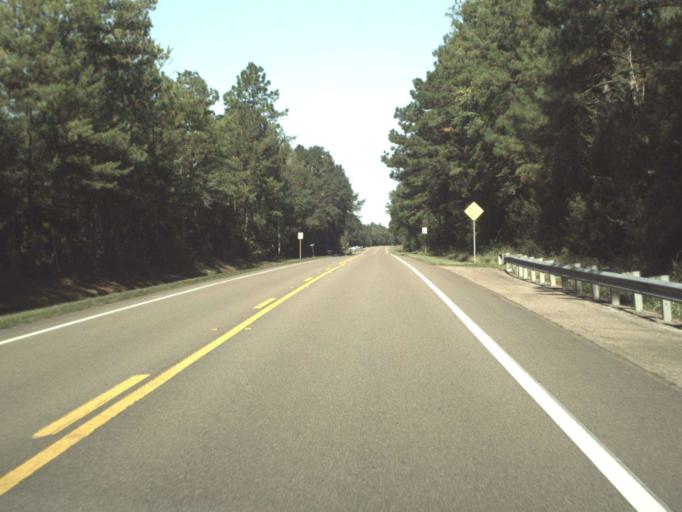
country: US
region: Florida
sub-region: Walton County
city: Freeport
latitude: 30.5781
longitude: -85.9295
